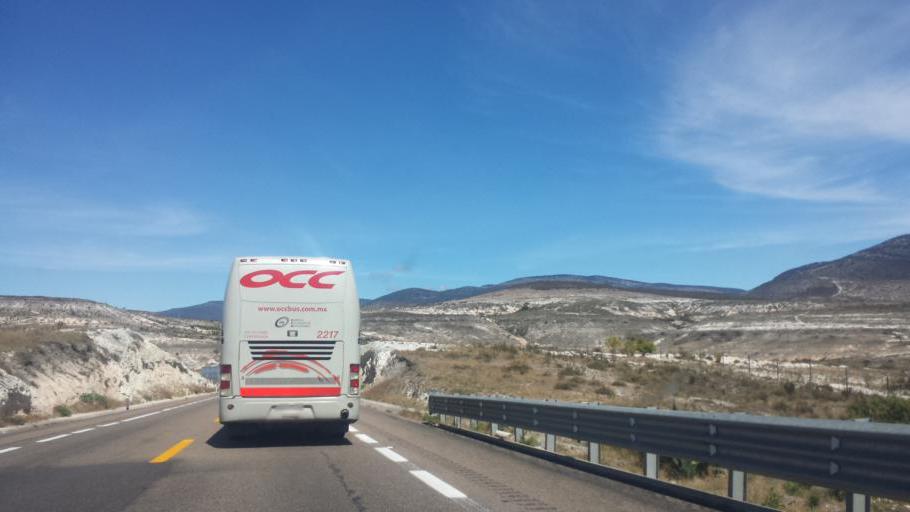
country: MX
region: Oaxaca
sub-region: Villa Tejupam de la Union
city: Villa Tejupam de la Union
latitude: 17.8979
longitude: -97.3685
